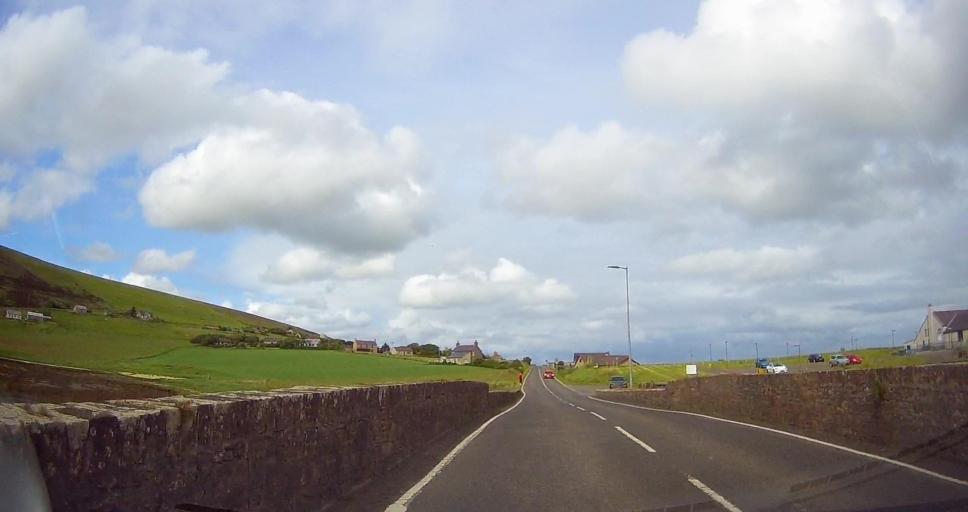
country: GB
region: Scotland
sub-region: Orkney Islands
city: Orkney
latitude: 59.0105
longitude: -3.1133
